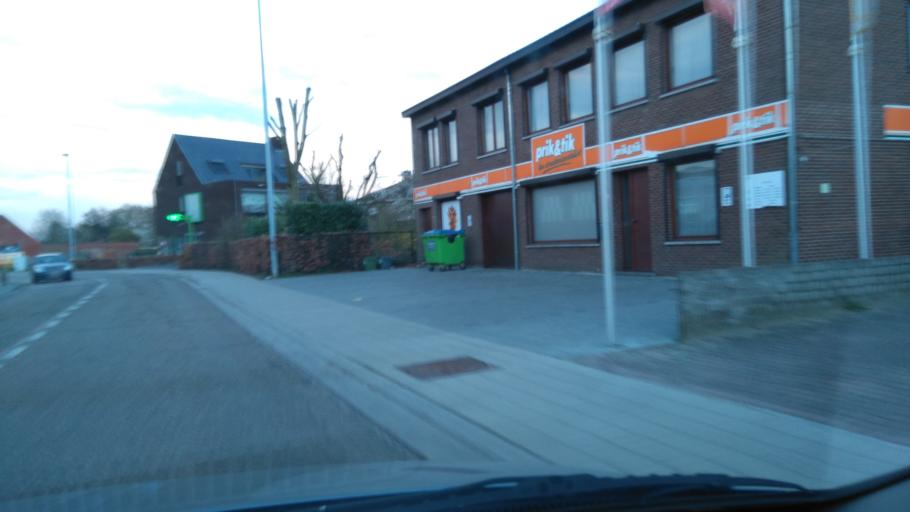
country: BE
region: Flanders
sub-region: Provincie Antwerpen
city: Turnhout
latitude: 51.3074
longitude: 4.9512
